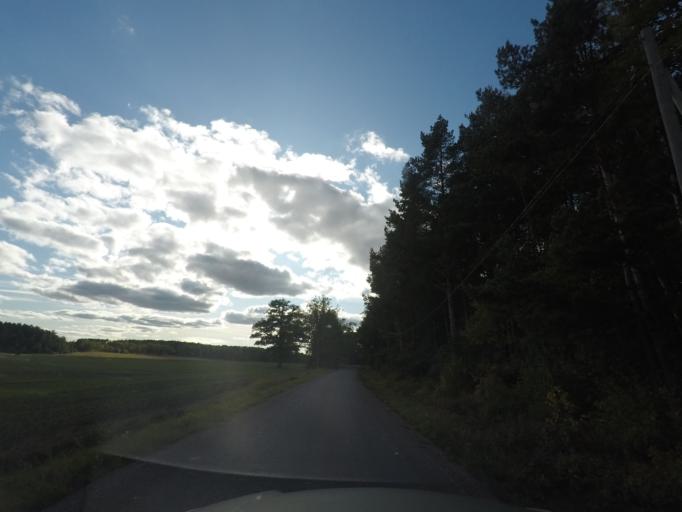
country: SE
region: Vaestmanland
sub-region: Hallstahammars Kommun
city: Kolback
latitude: 59.4891
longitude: 16.1905
